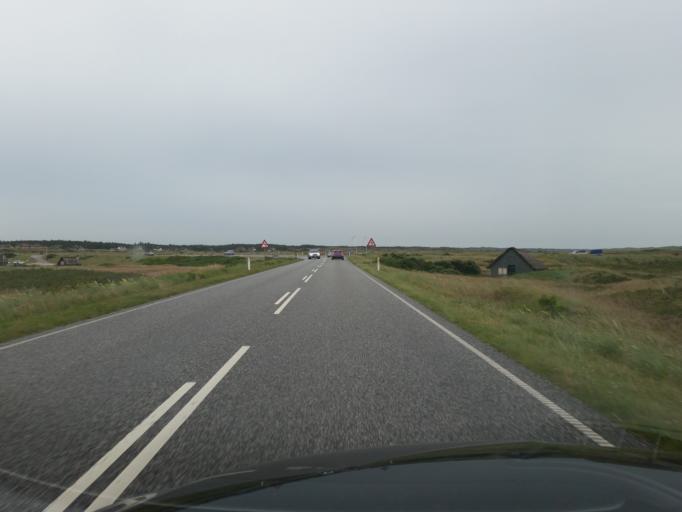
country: DK
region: Central Jutland
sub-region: Ringkobing-Skjern Kommune
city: Hvide Sande
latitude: 55.8204
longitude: 8.1816
